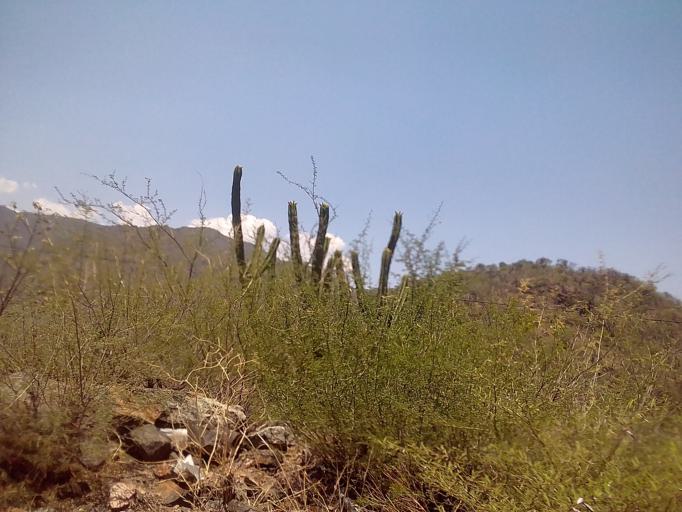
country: MX
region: Oaxaca
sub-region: San Pedro Quiatoni
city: San Pedro Quiatoni
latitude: 16.6777
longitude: -96.1487
